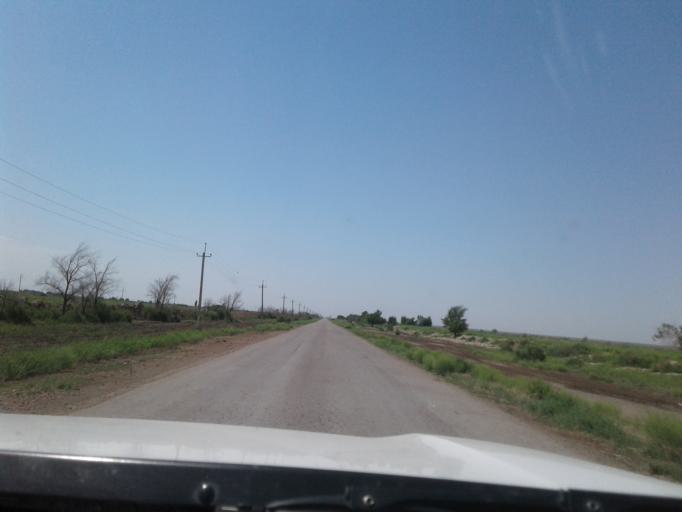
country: TM
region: Dasoguz
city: Koeneuergench
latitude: 41.8592
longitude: 58.7054
